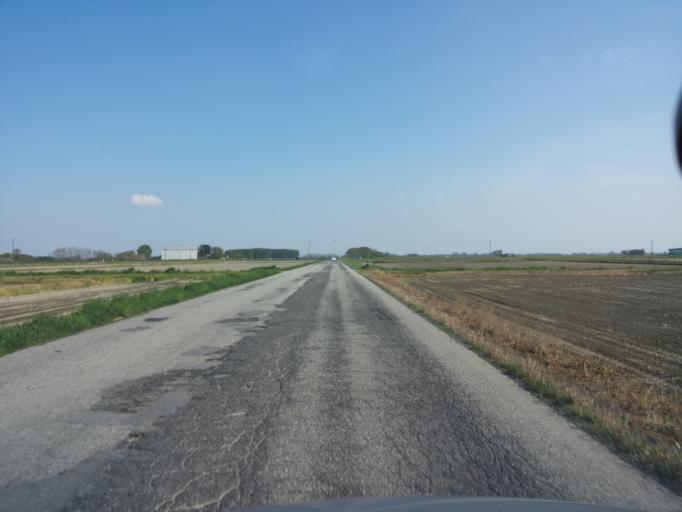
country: IT
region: Lombardy
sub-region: Provincia di Pavia
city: Cozzo
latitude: 45.1906
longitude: 8.5976
